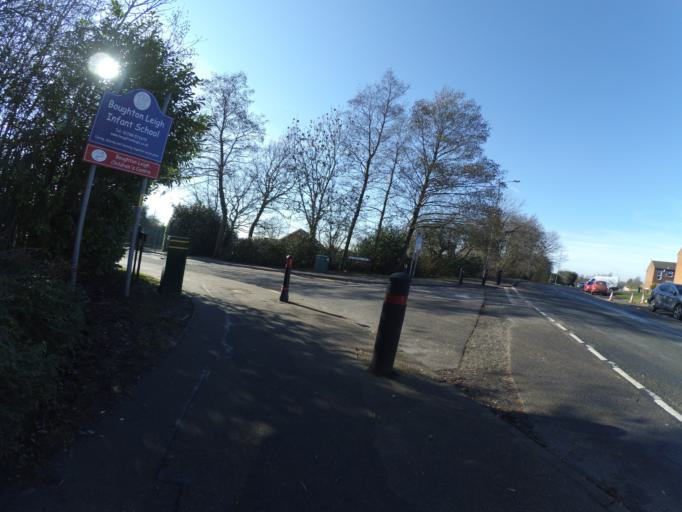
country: GB
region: England
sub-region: Warwickshire
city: Rugby
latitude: 52.3913
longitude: -1.2447
